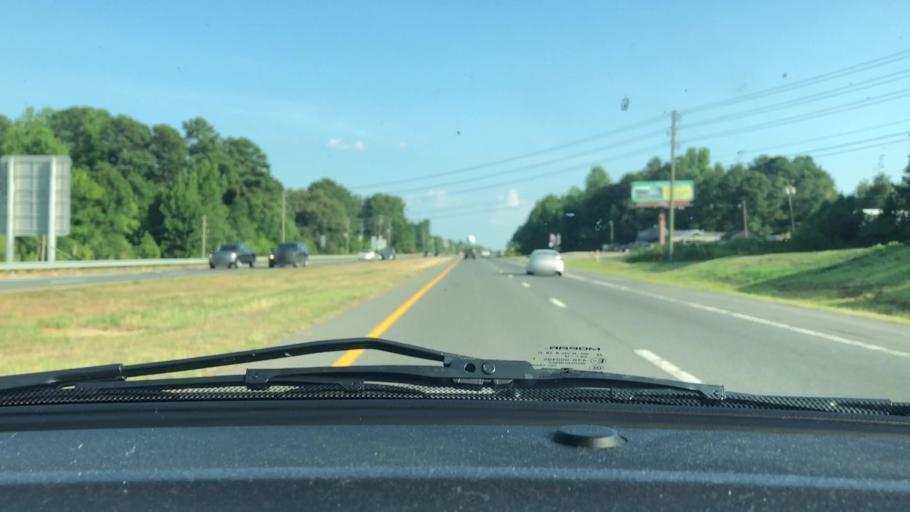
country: US
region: North Carolina
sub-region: Lee County
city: Broadway
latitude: 35.4275
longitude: -79.1218
